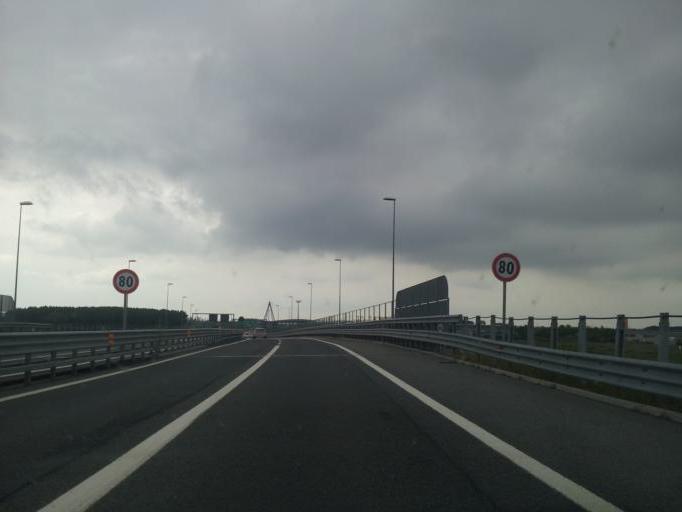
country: IT
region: Friuli Venezia Giulia
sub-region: Provincia di Udine
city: Ronchis
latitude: 45.8157
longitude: 13.0176
